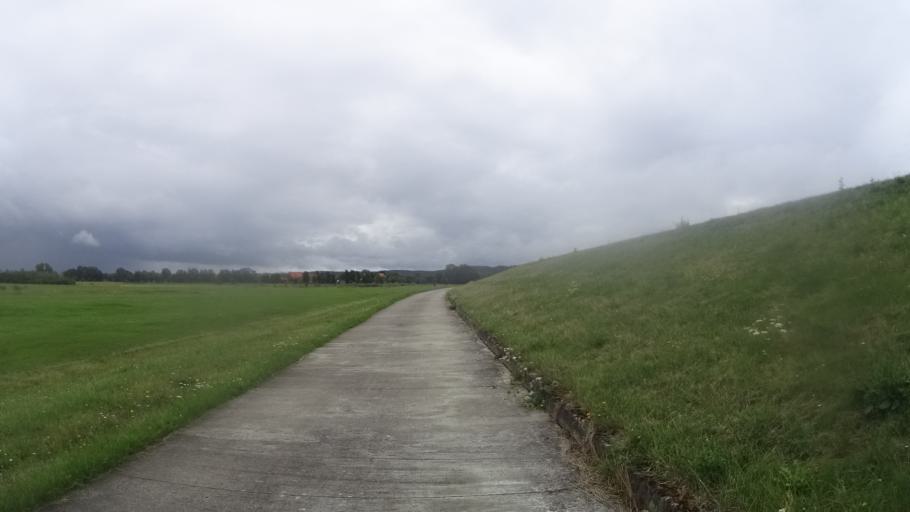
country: DE
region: Lower Saxony
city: Tosterglope
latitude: 53.2645
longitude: 10.8308
